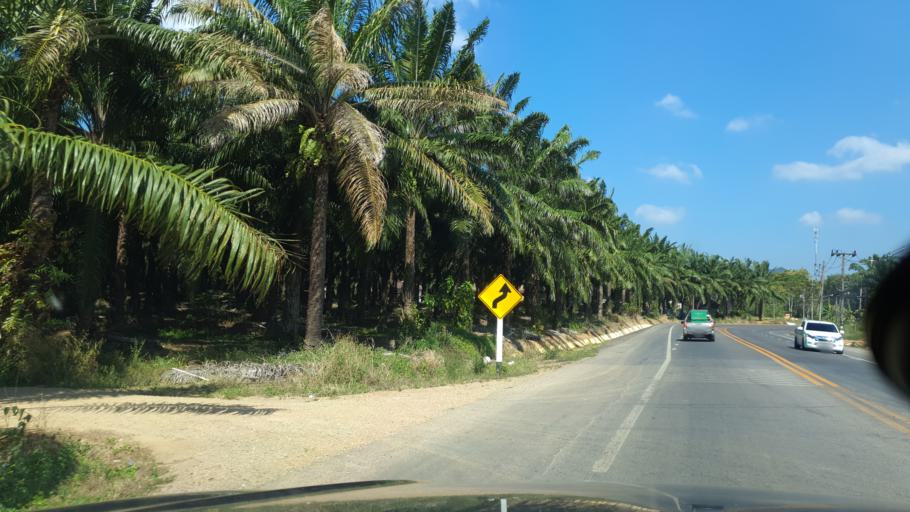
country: TH
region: Krabi
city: Krabi
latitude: 8.0676
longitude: 98.8589
